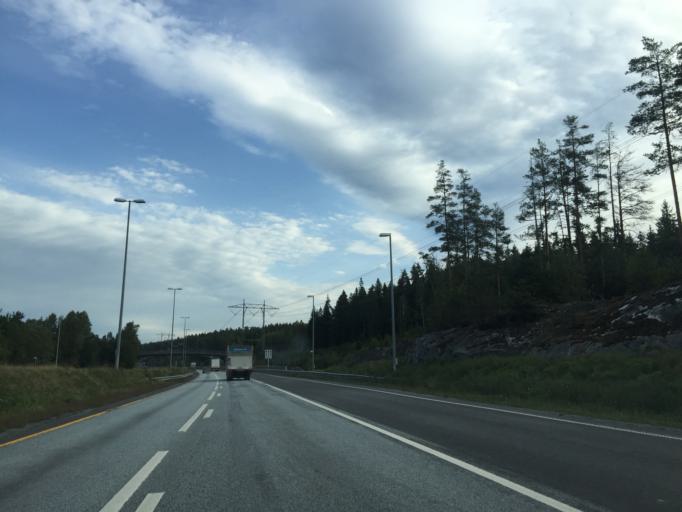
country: NO
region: Akershus
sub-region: Oppegard
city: Kolbotn
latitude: 59.7953
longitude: 10.8423
